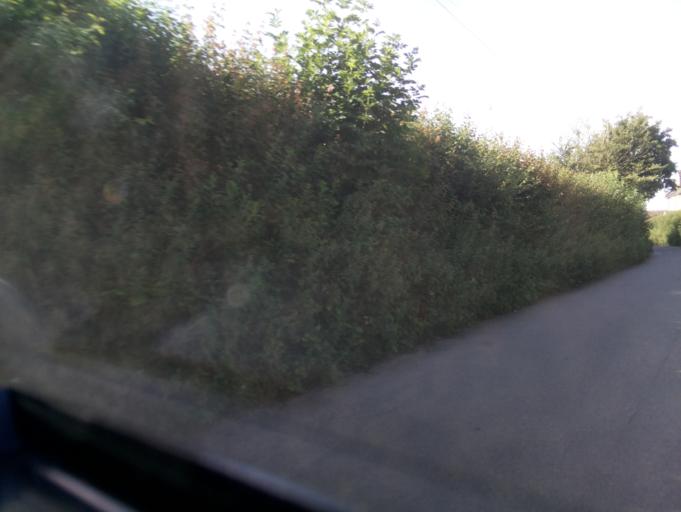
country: GB
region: England
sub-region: South Gloucestershire
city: Bitton
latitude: 51.4329
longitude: -2.4523
